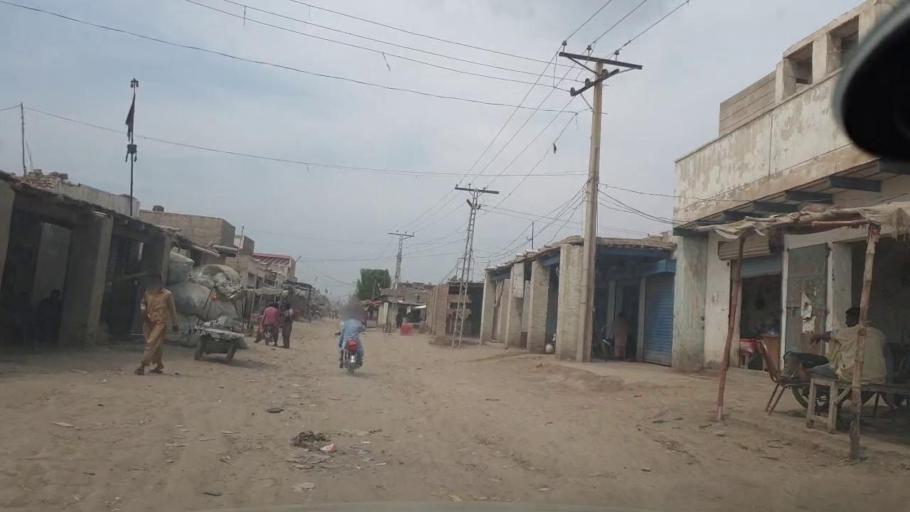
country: PK
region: Sindh
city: Jacobabad
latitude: 28.2655
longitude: 68.4377
